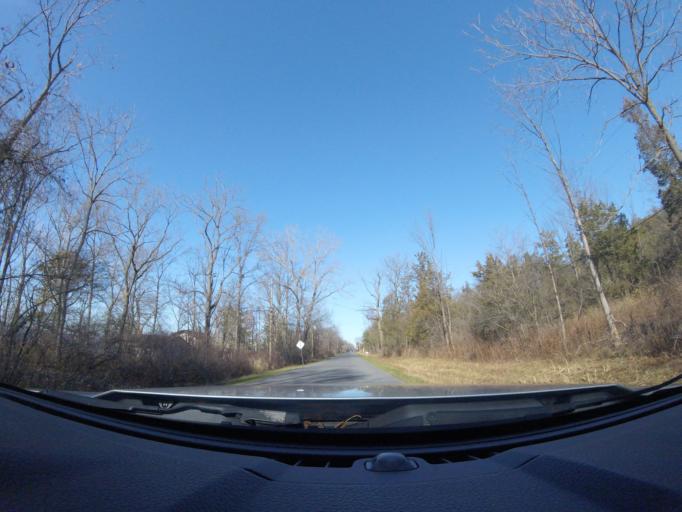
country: US
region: New York
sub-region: Cayuga County
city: Union Springs
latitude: 42.7216
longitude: -76.7081
